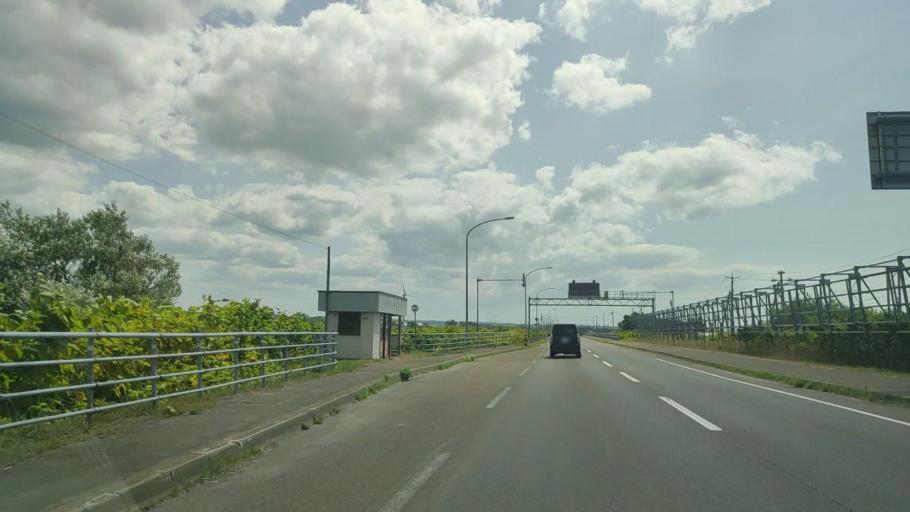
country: JP
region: Hokkaido
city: Makubetsu
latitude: 44.7551
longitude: 141.7948
